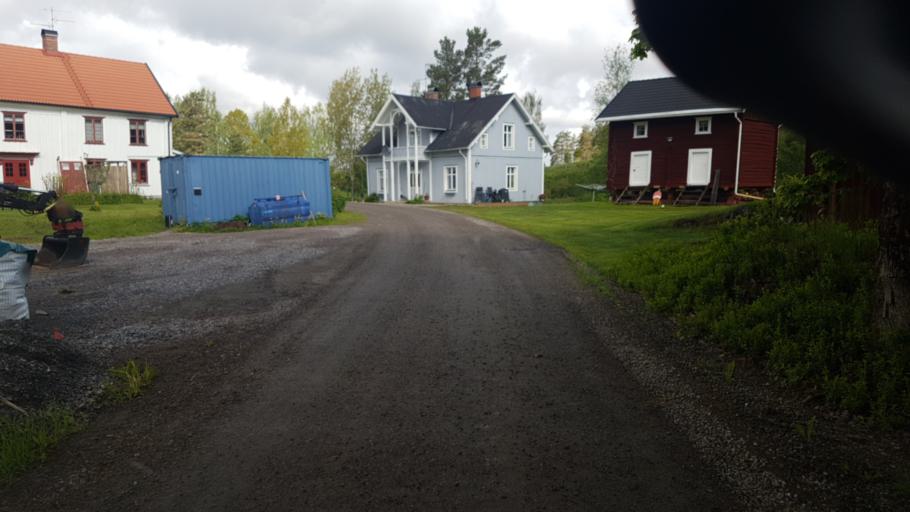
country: NO
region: Hedmark
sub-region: Eidskog
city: Skotterud
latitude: 59.8549
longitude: 11.9795
